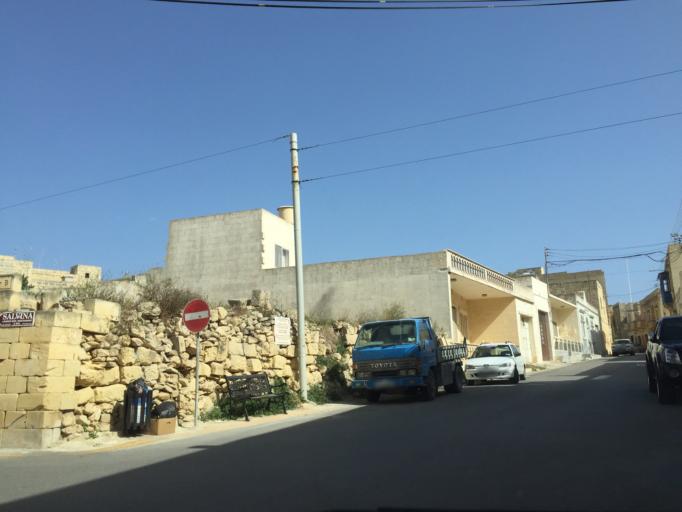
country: MT
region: L-Gharb
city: Gharb
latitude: 36.0630
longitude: 14.2073
